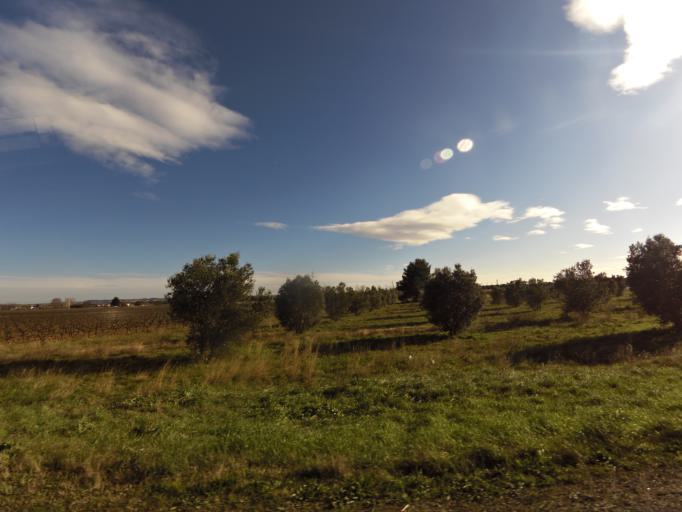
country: FR
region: Languedoc-Roussillon
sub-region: Departement du Gard
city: Vestric-et-Candiac
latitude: 43.7391
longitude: 4.2424
